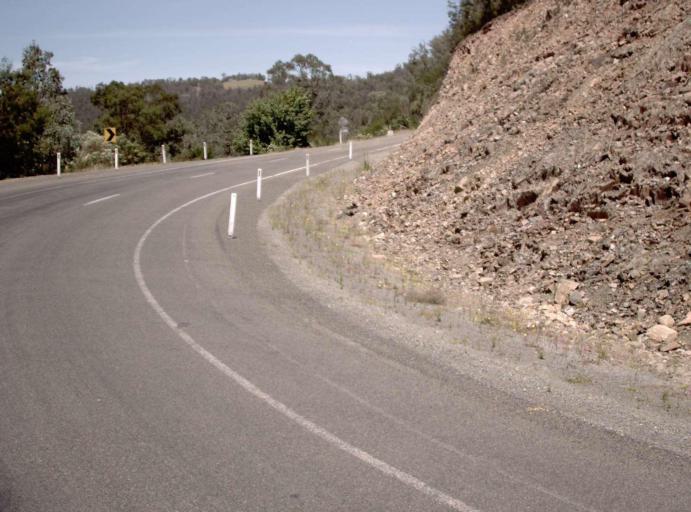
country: AU
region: Victoria
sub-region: East Gippsland
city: Bairnsdale
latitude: -37.4748
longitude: 147.8333
